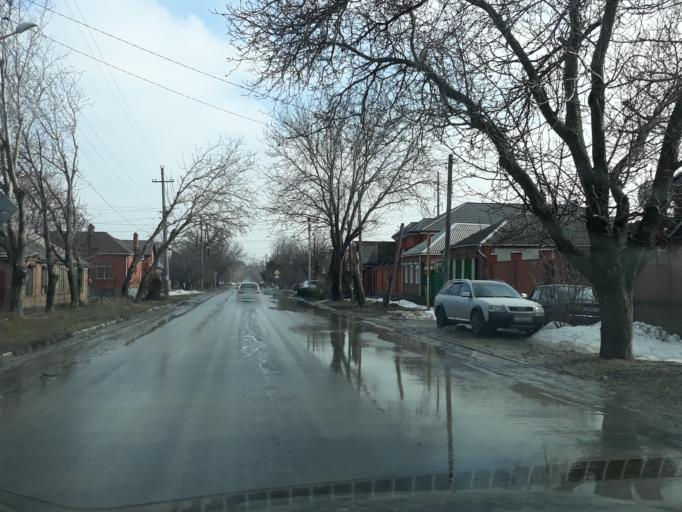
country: RU
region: Rostov
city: Taganrog
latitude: 47.2142
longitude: 38.9033
